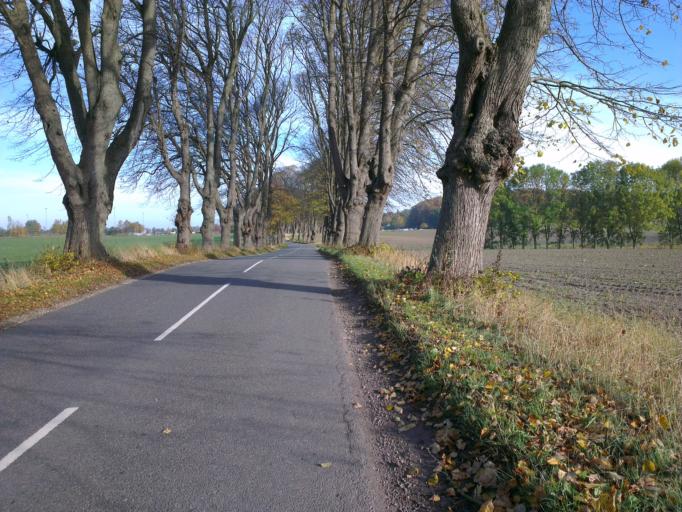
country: DK
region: Capital Region
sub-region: Frederikssund Kommune
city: Skibby
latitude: 55.7866
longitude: 11.9439
